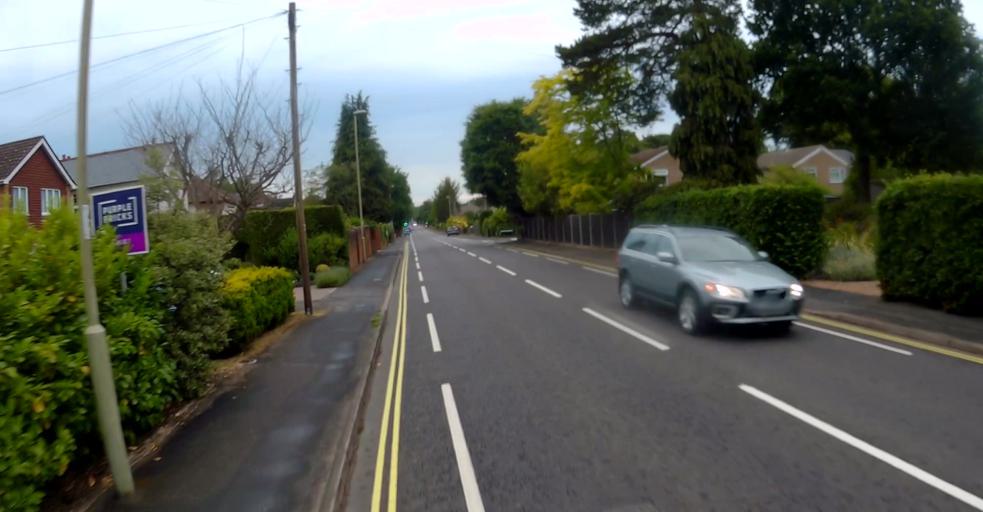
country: GB
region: England
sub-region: Hampshire
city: Fleet
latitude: 51.2778
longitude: -0.8231
